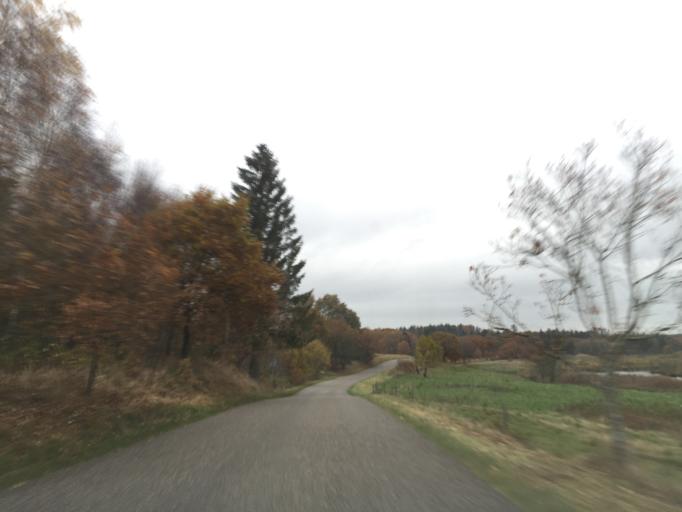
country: DK
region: Central Jutland
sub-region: Silkeborg Kommune
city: Svejbaek
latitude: 56.1971
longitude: 9.6470
